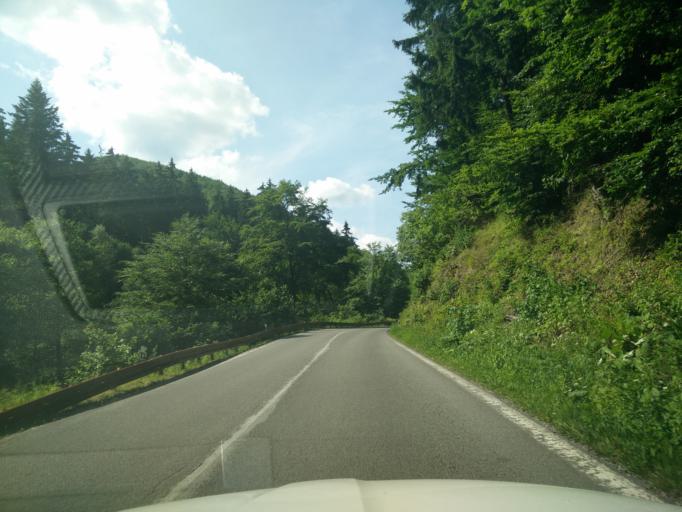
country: SK
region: Zilinsky
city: Rajec
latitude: 48.9419
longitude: 18.6288
